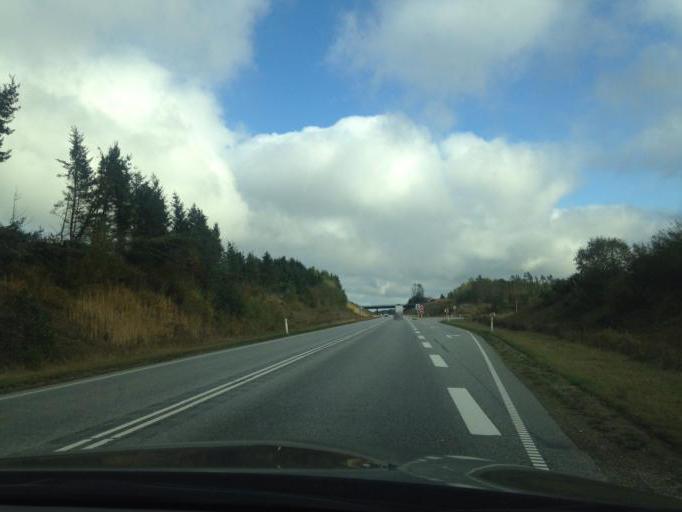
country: DK
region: South Denmark
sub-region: Vejle Kommune
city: Give
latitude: 55.8228
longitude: 9.2486
